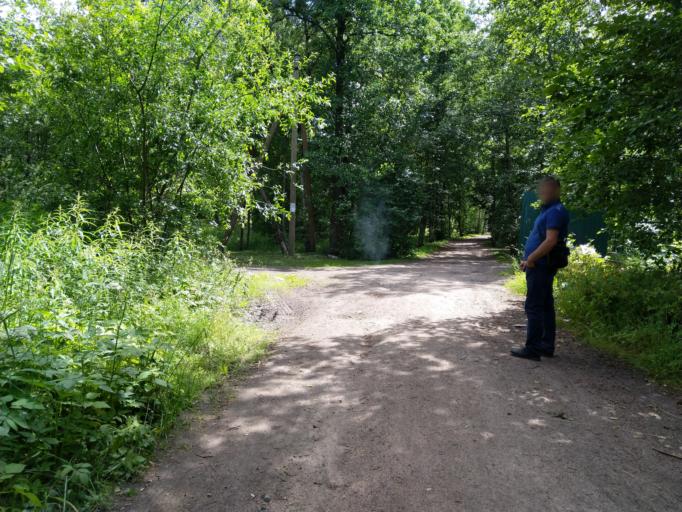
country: RU
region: Leningrad
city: Sapernoye
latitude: 60.6800
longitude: 30.0088
